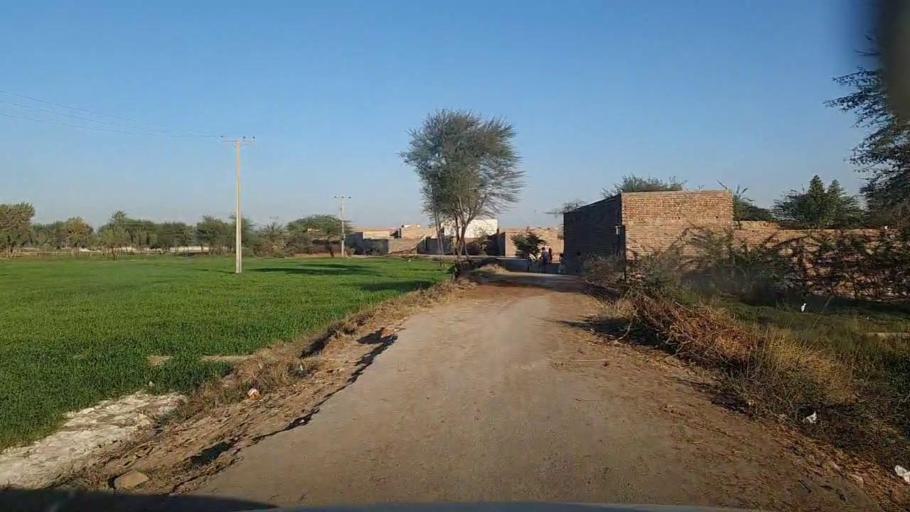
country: PK
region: Sindh
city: Khairpur
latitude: 28.0430
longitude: 69.7105
